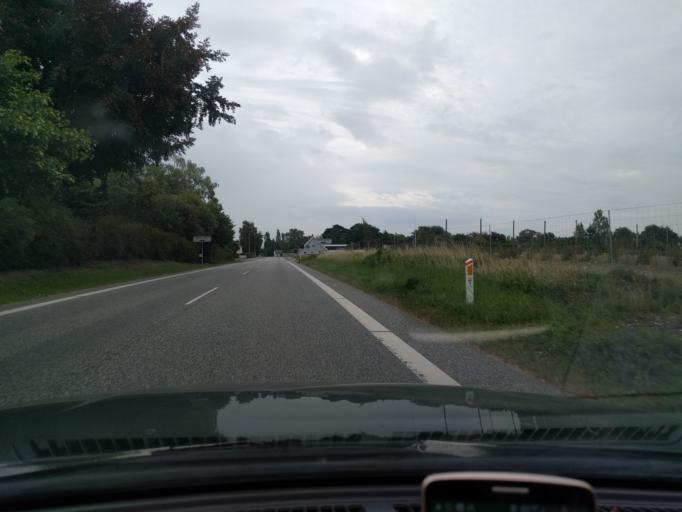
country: DK
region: Zealand
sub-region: Slagelse Kommune
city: Skaelskor
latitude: 55.2393
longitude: 11.4221
